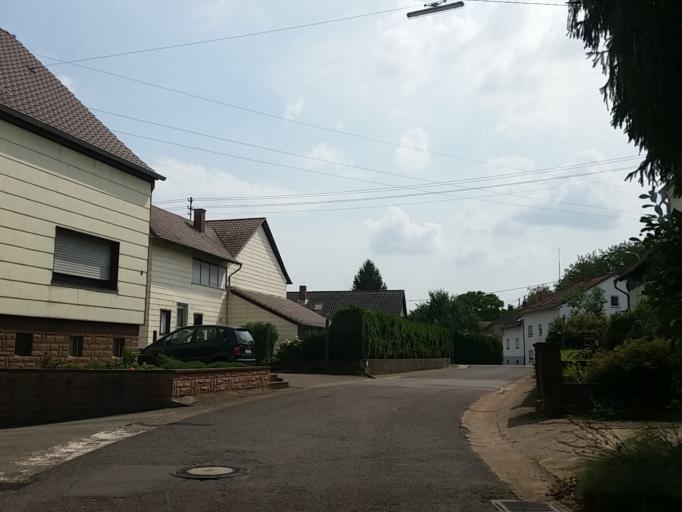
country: DE
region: Saarland
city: Schmelz
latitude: 49.4305
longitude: 6.8450
